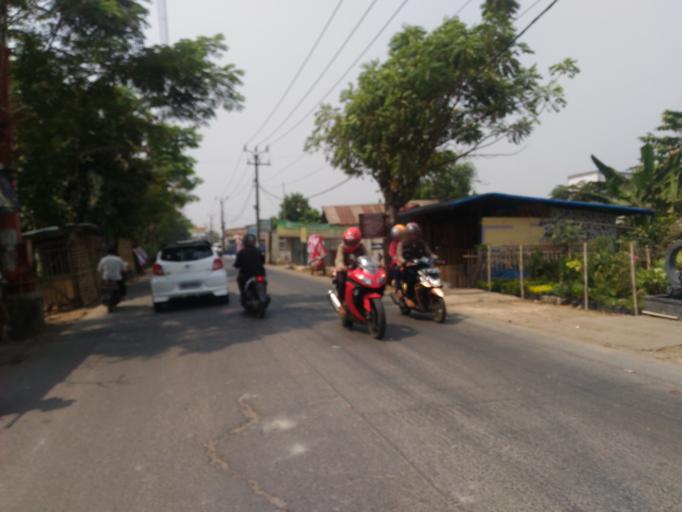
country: ID
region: West Java
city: Sepatan
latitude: -6.1479
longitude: 106.5798
